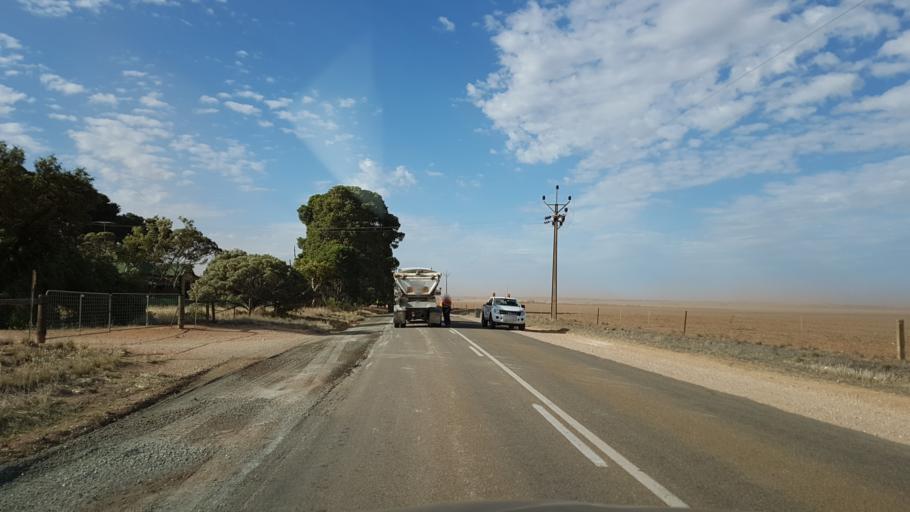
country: AU
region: South Australia
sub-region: Clare and Gilbert Valleys
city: Clare
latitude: -33.8808
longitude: 138.4792
